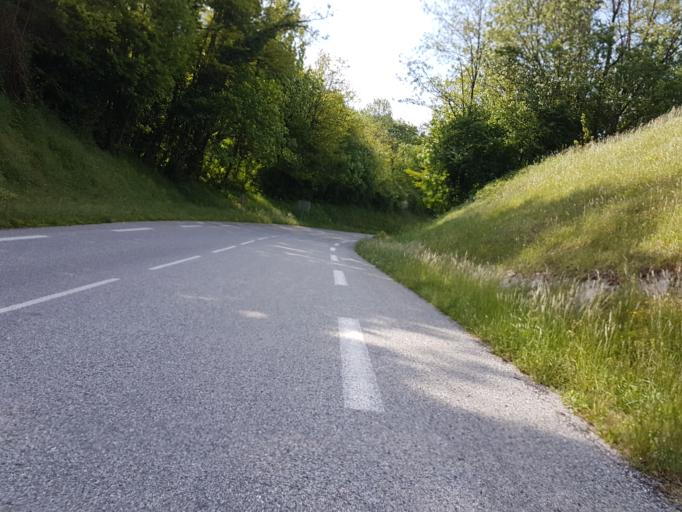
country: FR
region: Rhone-Alpes
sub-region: Departement de la Haute-Savoie
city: Moye
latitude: 45.9118
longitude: 5.8394
